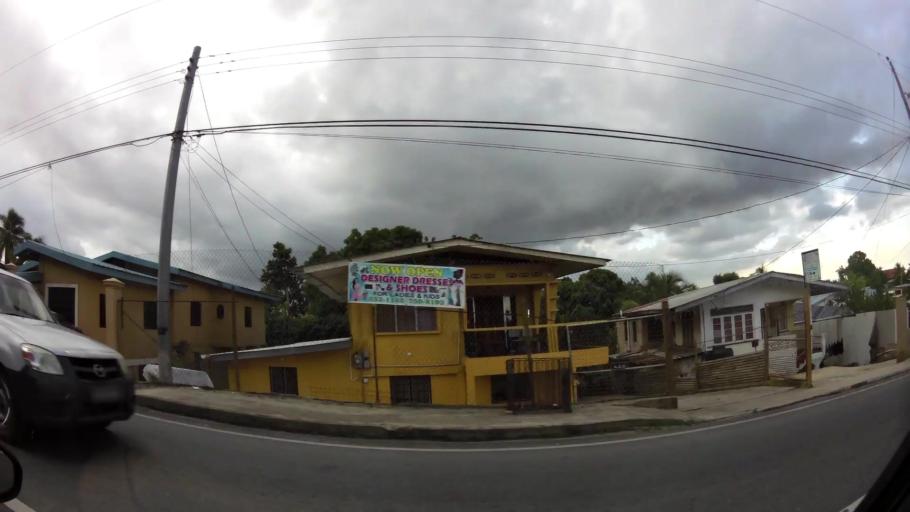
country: TT
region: City of San Fernando
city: Mon Repos
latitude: 10.2504
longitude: -61.4370
